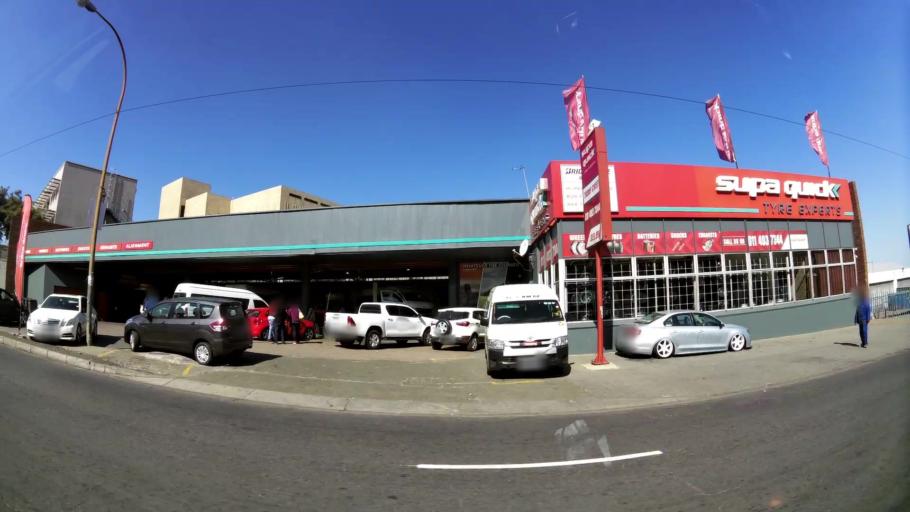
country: ZA
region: Gauteng
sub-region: City of Johannesburg Metropolitan Municipality
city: Johannesburg
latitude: -26.2135
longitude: 28.0359
